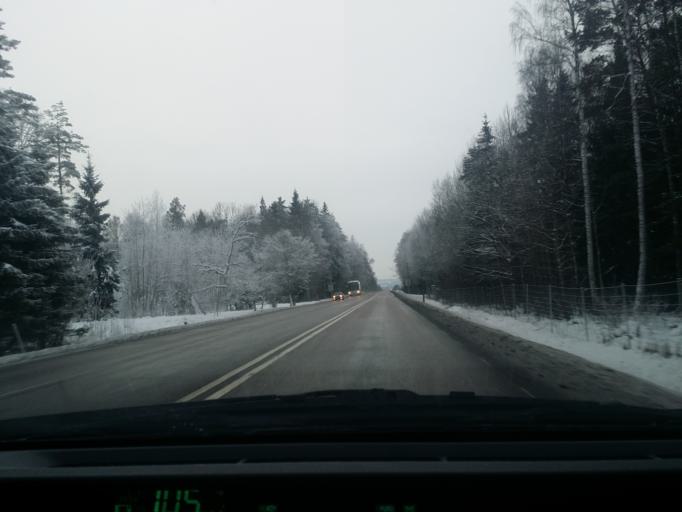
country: SE
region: Vaestra Goetaland
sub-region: Gullspangs Kommun
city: Anderstorp
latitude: 58.8776
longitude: 14.2652
